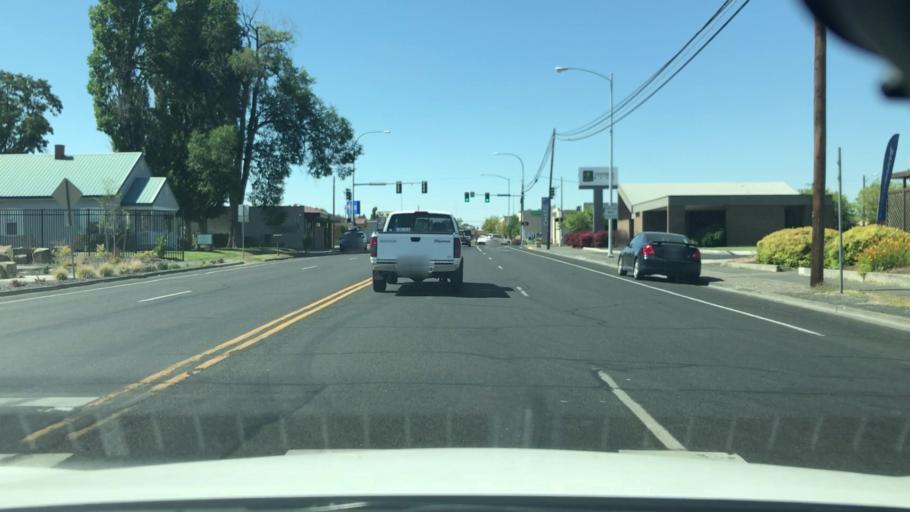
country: US
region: Washington
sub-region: Grant County
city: Moses Lake
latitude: 47.1286
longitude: -119.2764
